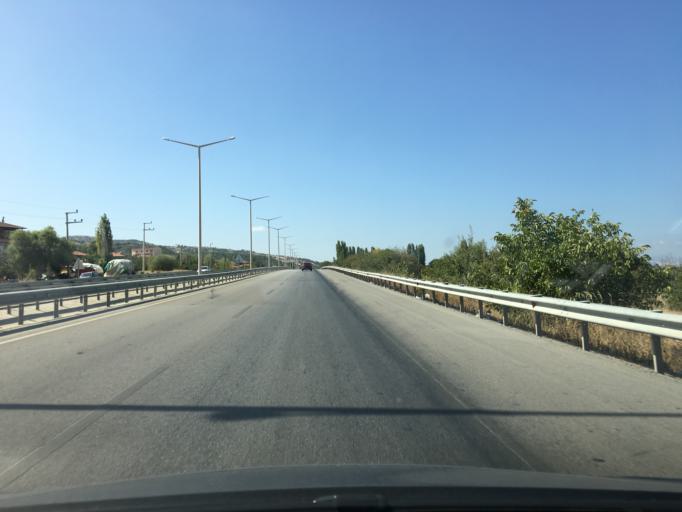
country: TR
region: Burdur
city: Burdur
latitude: 37.7623
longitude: 30.3467
